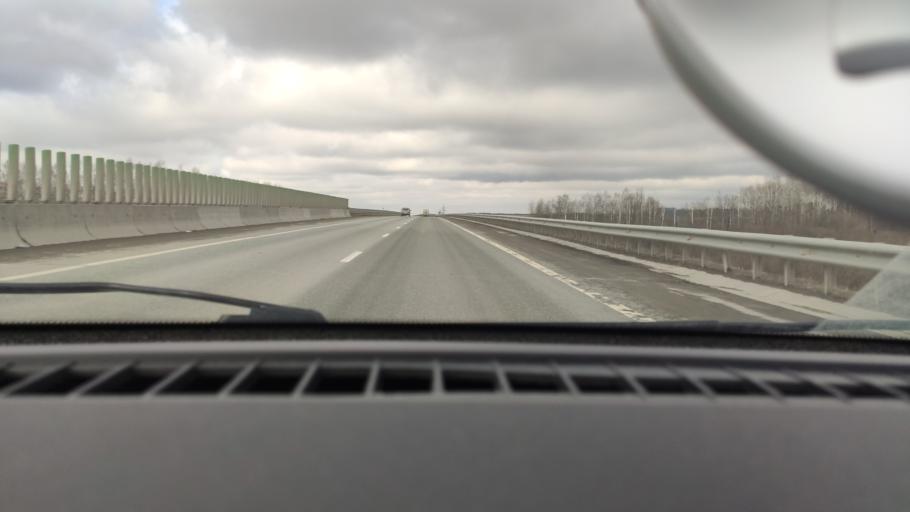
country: RU
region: Perm
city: Froly
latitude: 57.9313
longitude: 56.3009
